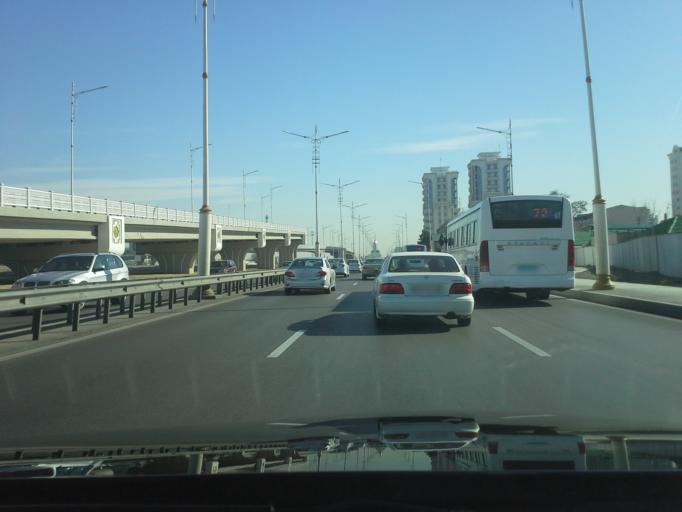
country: TM
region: Ahal
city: Ashgabat
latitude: 37.9489
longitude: 58.3845
